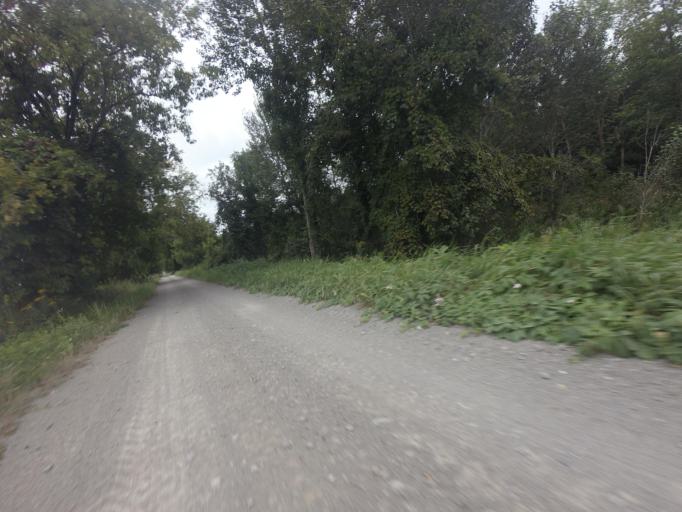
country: CA
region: Ontario
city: Omemee
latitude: 44.4696
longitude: -78.7521
